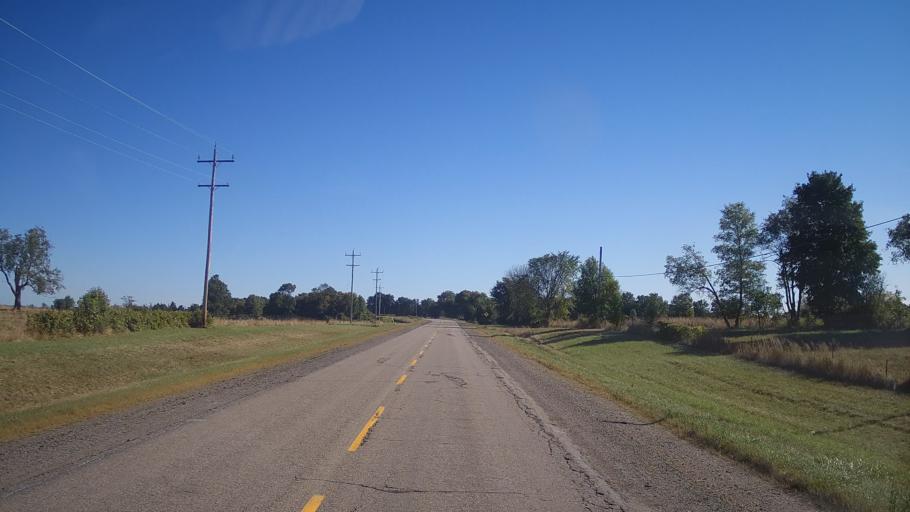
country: CA
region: Ontario
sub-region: Lanark County
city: Smiths Falls
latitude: 44.6154
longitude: -76.0502
